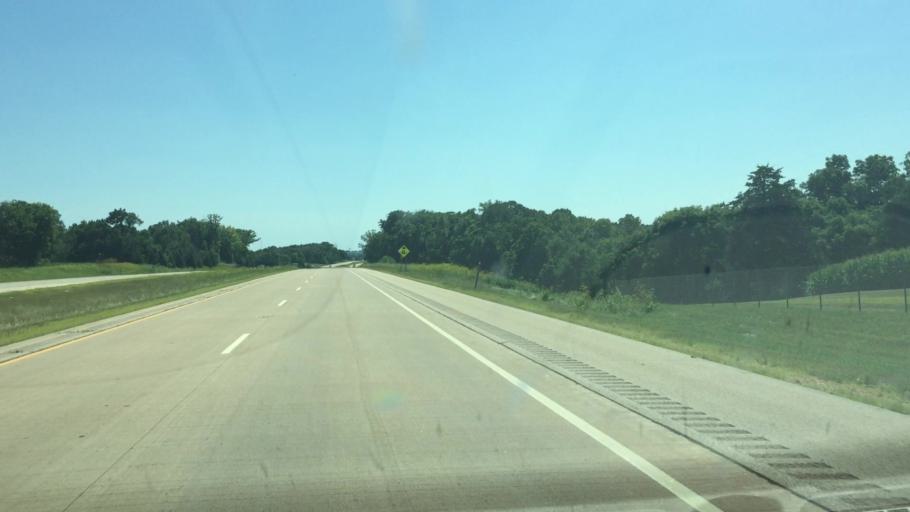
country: US
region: Wisconsin
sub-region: Grant County
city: Platteville
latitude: 42.6868
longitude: -90.5343
